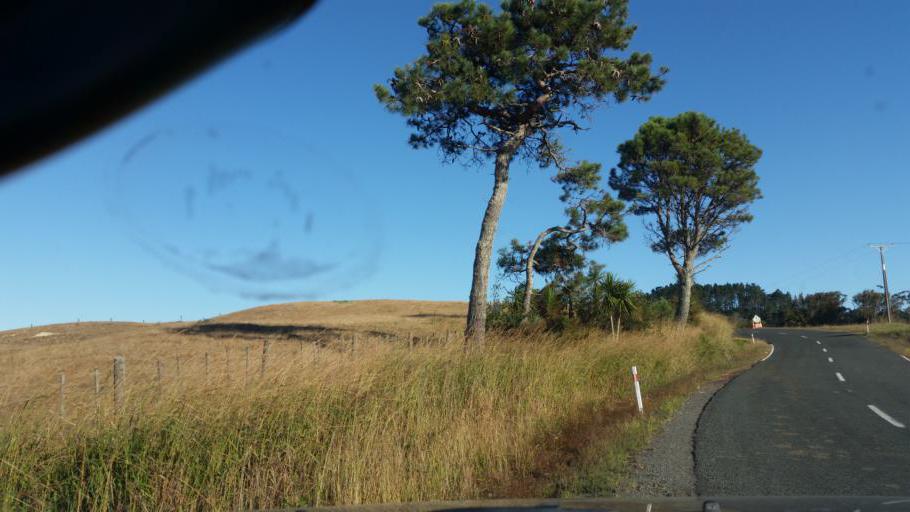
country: NZ
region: Northland
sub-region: Kaipara District
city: Dargaville
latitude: -36.1035
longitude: 174.1731
